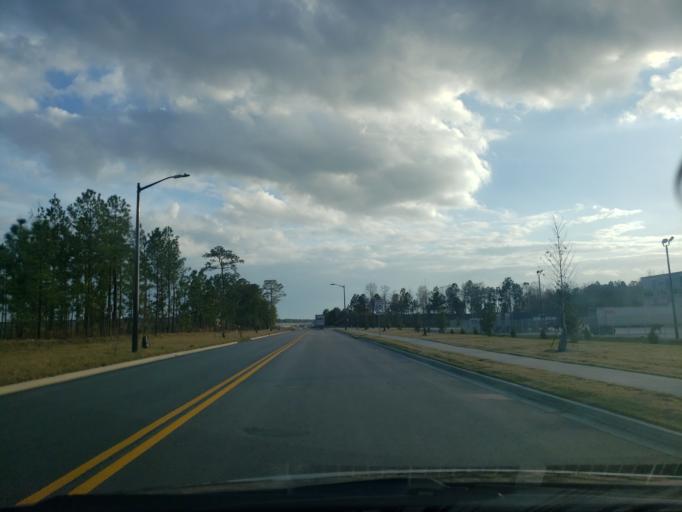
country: US
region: Georgia
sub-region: Chatham County
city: Bloomingdale
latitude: 32.1710
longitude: -81.2701
